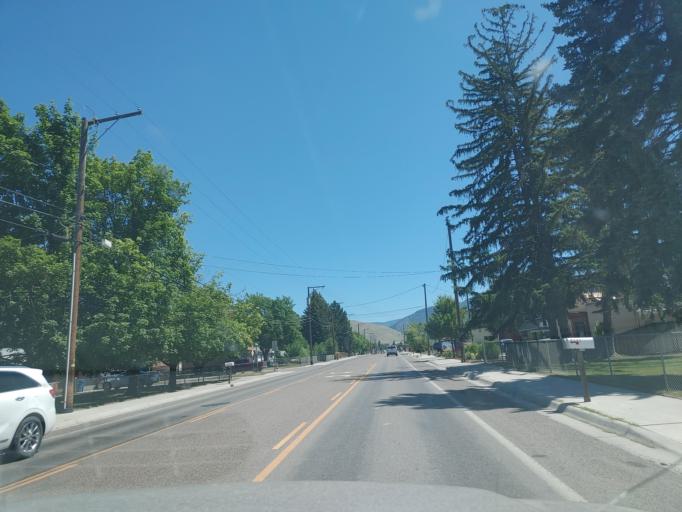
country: US
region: Montana
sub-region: Missoula County
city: Orchard Homes
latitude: 46.8669
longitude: -114.0358
